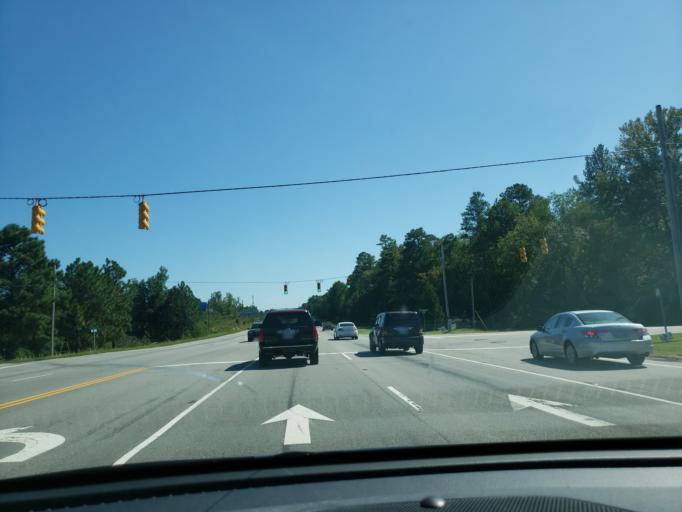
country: US
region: North Carolina
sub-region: Lee County
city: Broadway
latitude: 35.3599
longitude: -79.1099
